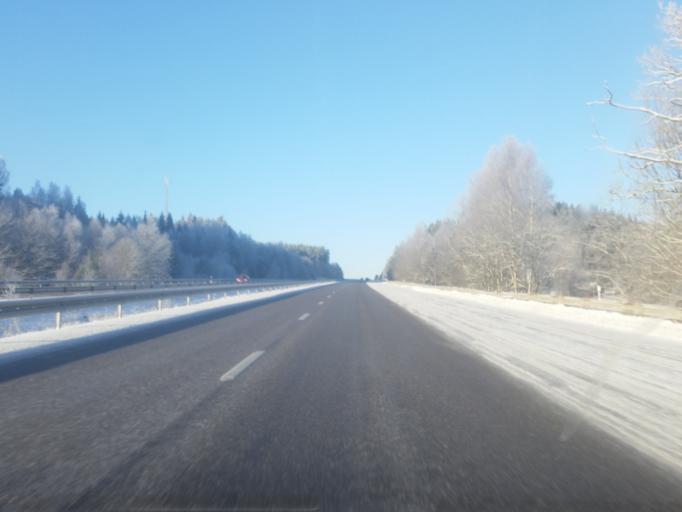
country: SE
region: Vaestra Goetaland
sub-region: Bollebygds Kommun
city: Bollebygd
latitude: 57.6657
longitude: 12.5359
